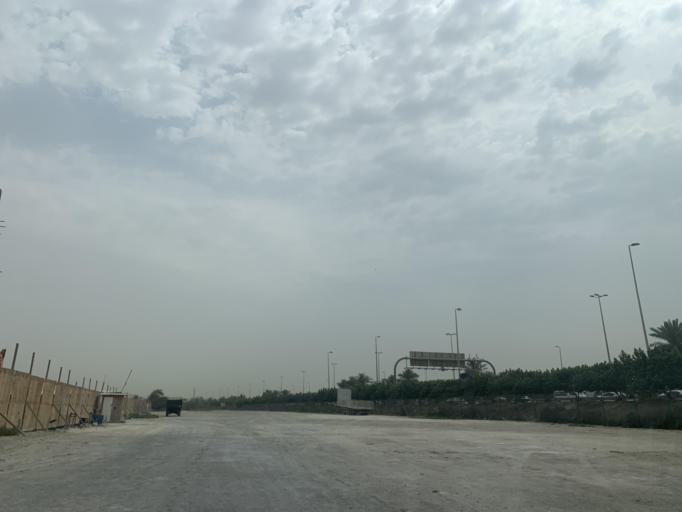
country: BH
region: Northern
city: Madinat `Isa
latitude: 26.1765
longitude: 50.5029
